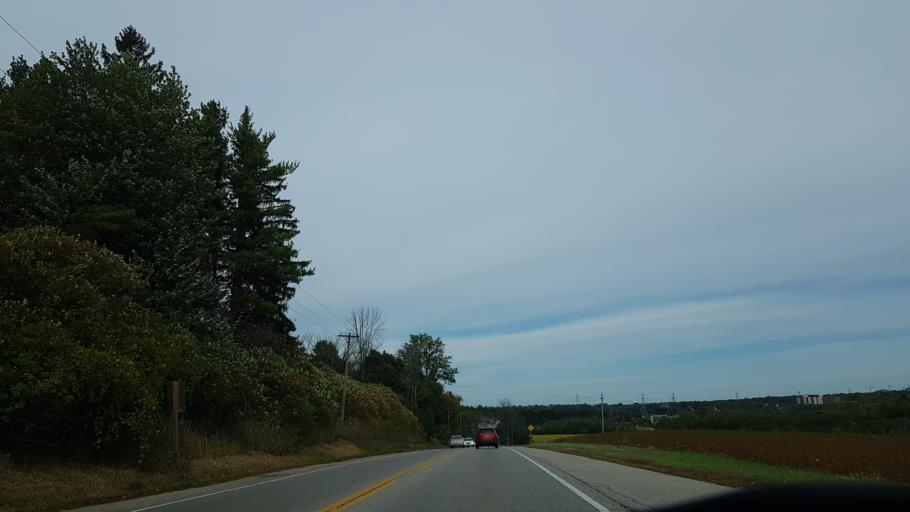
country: CA
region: Ontario
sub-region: Wellington County
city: Guelph
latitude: 43.5106
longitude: -80.2665
